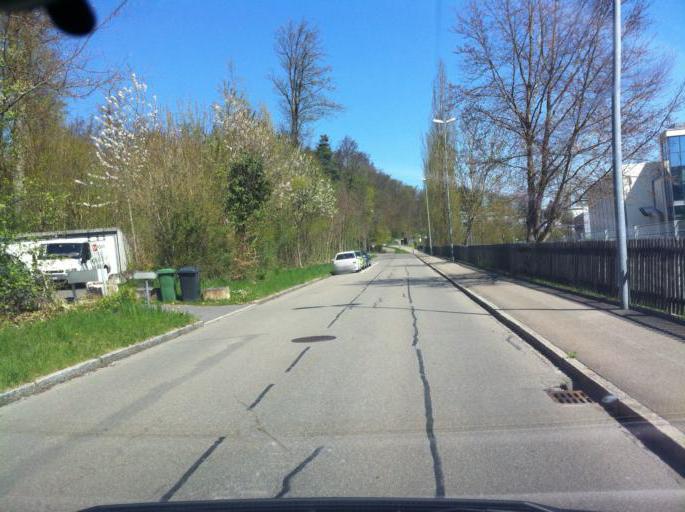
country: CH
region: Schaffhausen
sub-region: Bezirk Schaffhausen
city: Schaffhausen
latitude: 47.7118
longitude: 8.6386
